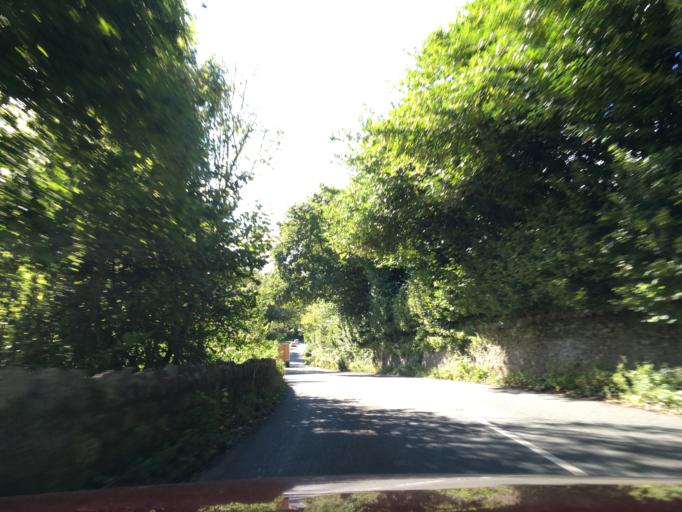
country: GB
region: England
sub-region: Devon
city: South Brent
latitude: 50.4315
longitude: -3.7846
